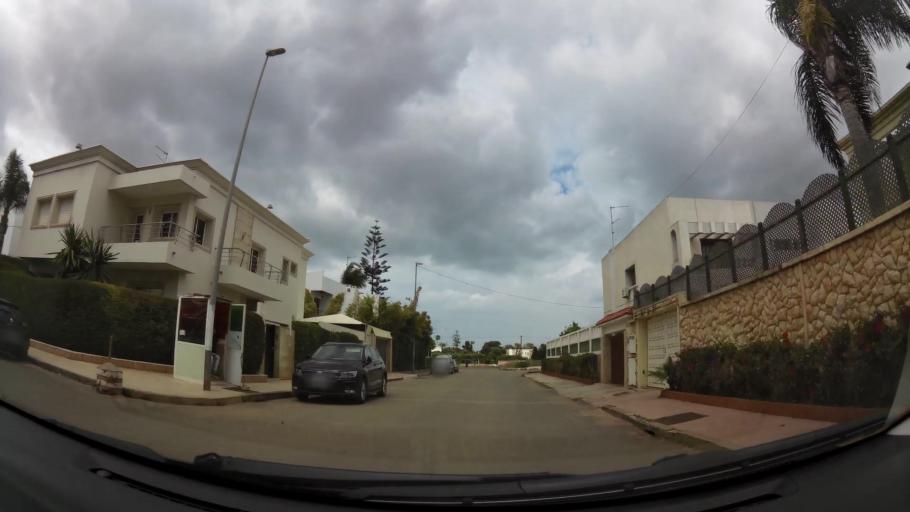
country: MA
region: Grand Casablanca
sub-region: Casablanca
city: Casablanca
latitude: 33.5798
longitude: -7.6506
